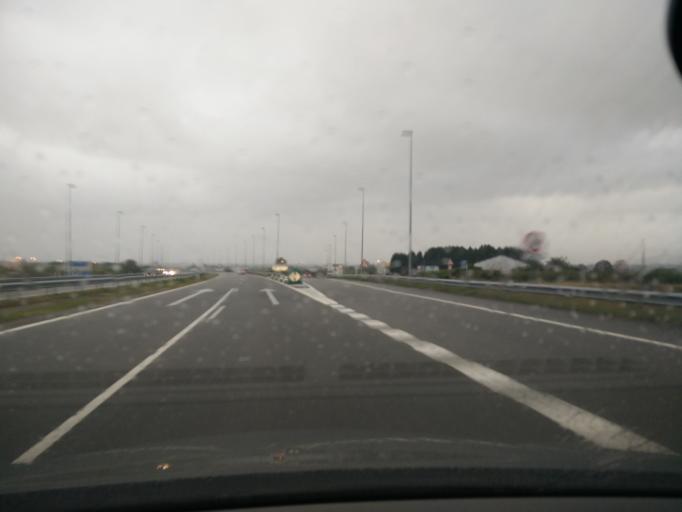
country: ES
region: Asturias
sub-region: Province of Asturias
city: Figueras
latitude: 43.5430
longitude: -7.0252
